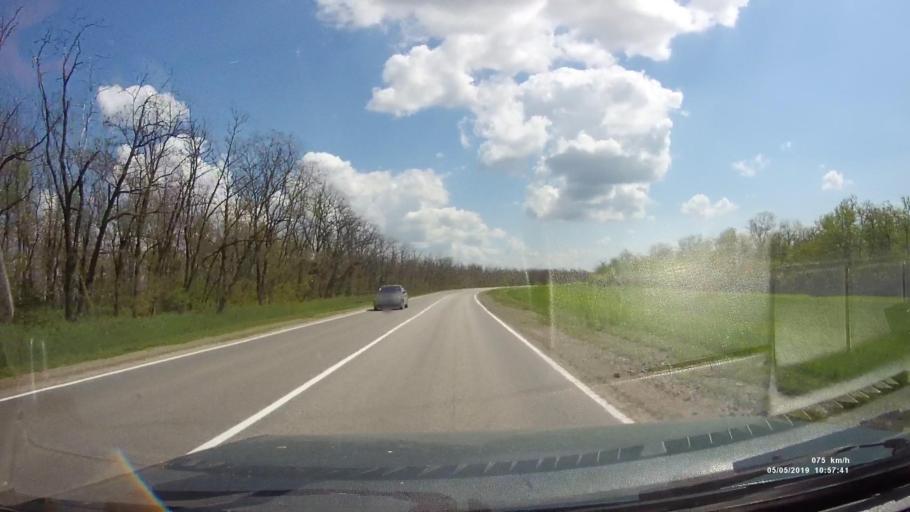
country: RU
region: Rostov
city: Ust'-Donetskiy
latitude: 47.6716
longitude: 40.8401
